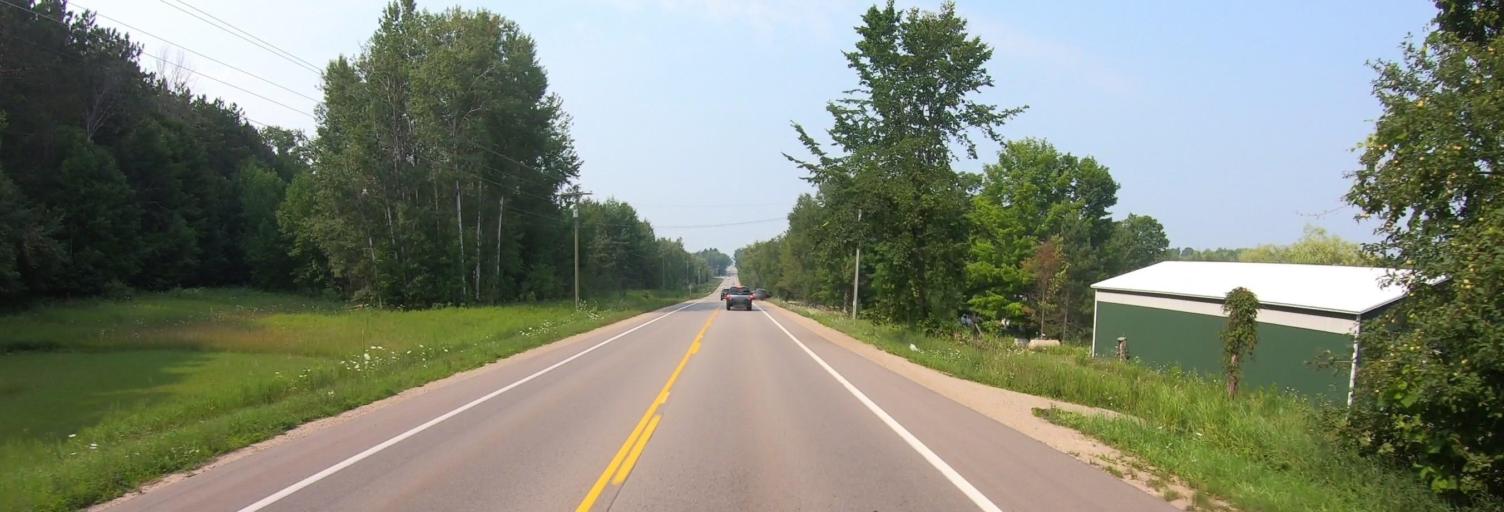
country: US
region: Michigan
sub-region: Charlevoix County
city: Charlevoix
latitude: 45.2150
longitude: -85.2614
